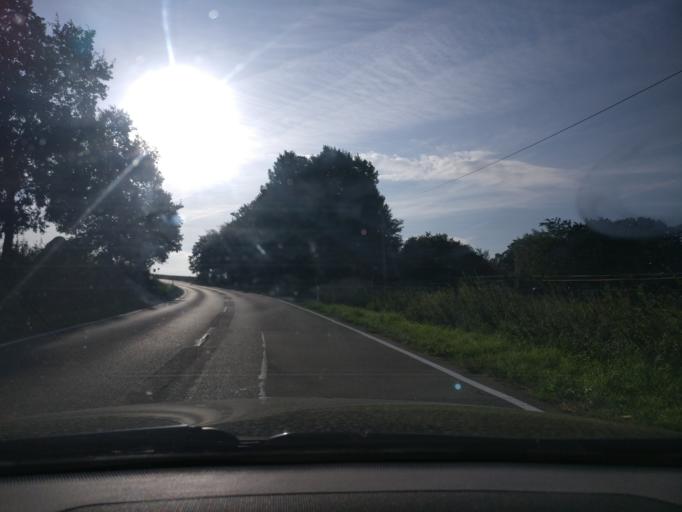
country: DE
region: Lower Saxony
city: Melle
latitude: 52.1963
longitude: 8.2622
